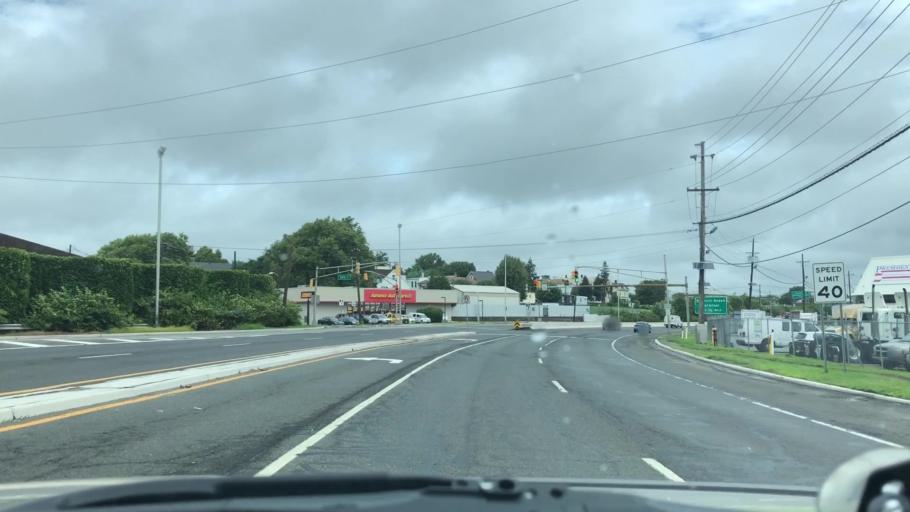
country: US
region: New Jersey
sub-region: Hudson County
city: Bayonne
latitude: 40.6660
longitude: -74.1086
